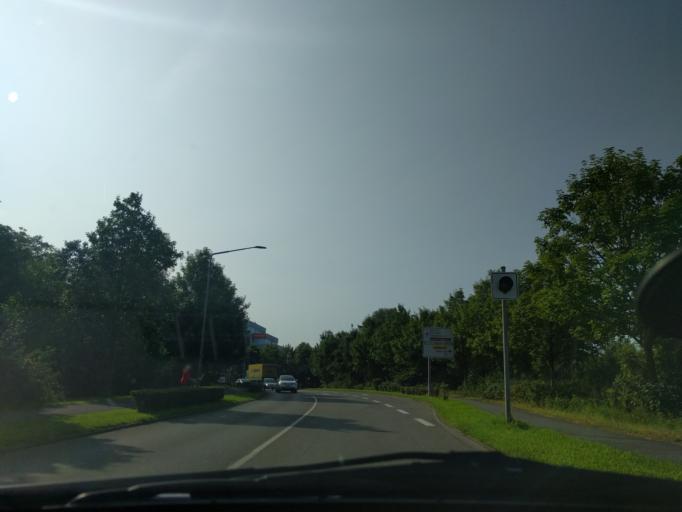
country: DE
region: North Rhine-Westphalia
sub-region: Regierungsbezirk Dusseldorf
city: Ratingen
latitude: 51.3023
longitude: 6.8391
